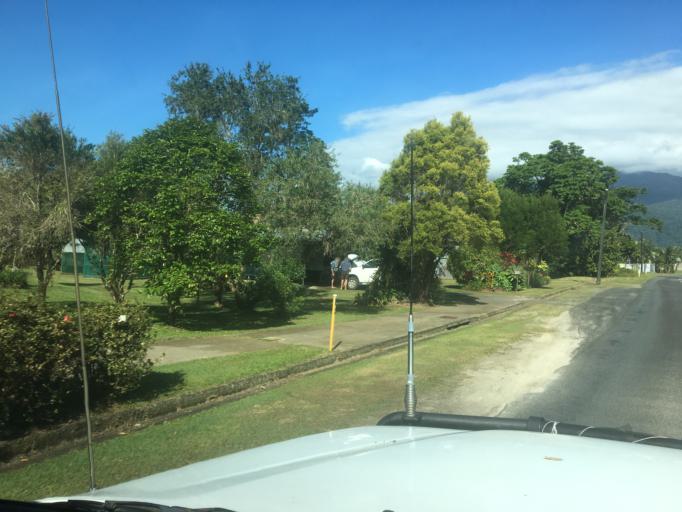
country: AU
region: Queensland
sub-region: Cassowary Coast
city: Innisfail
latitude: -17.3469
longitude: 145.9076
